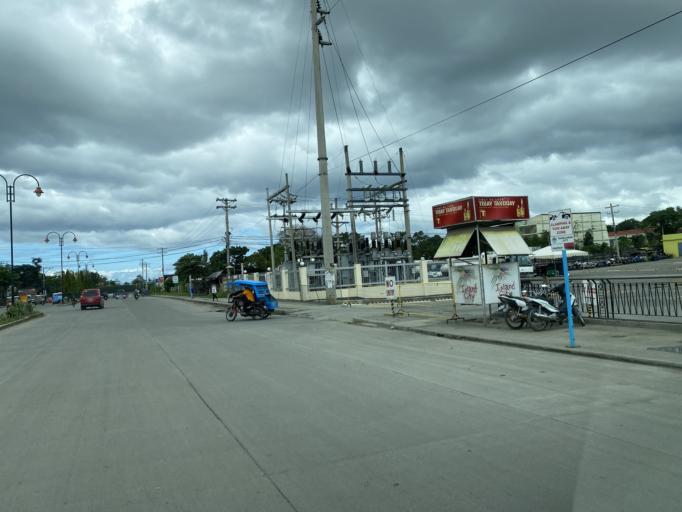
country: PH
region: Central Visayas
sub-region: Province of Bohol
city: Tagbilaran City
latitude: 9.6547
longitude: 123.8688
